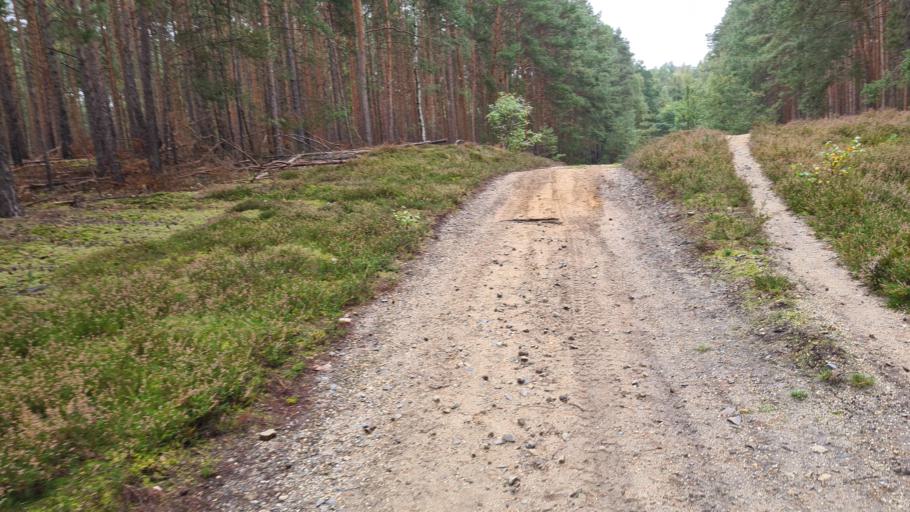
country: DE
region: Brandenburg
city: Schonewalde
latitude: 51.6314
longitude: 13.6212
